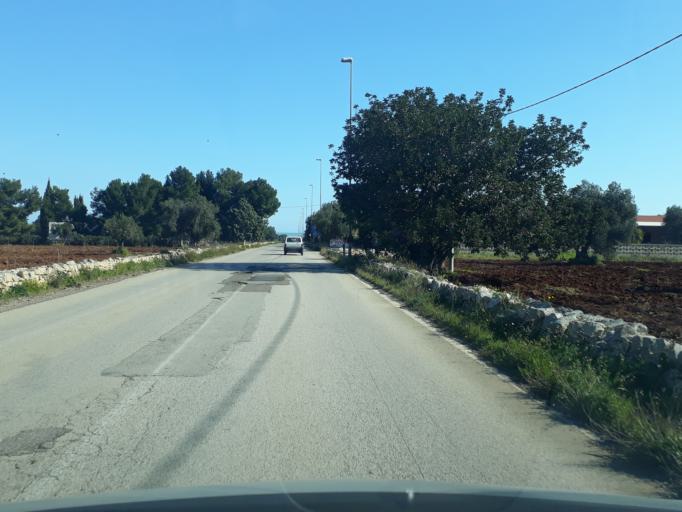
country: IT
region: Apulia
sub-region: Provincia di Brindisi
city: Fasano
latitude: 40.9000
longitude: 17.3405
